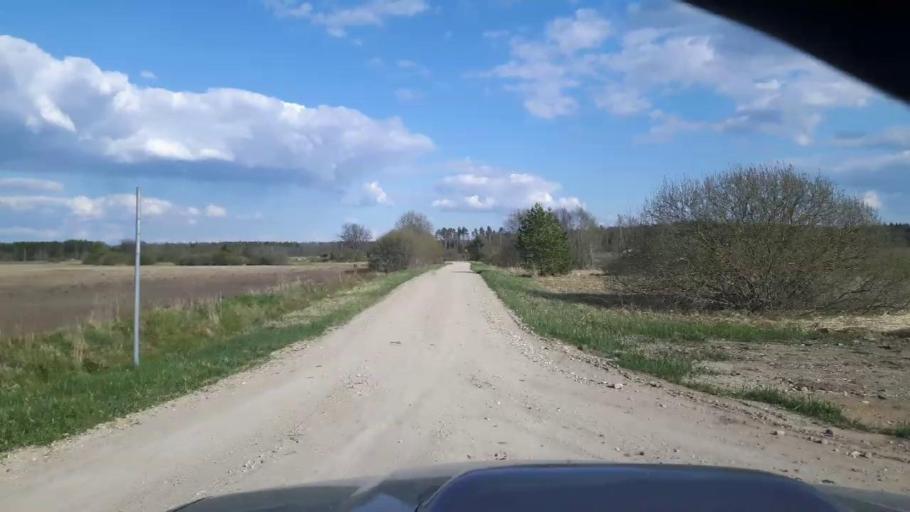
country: EE
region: Paernumaa
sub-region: Tootsi vald
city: Tootsi
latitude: 58.4139
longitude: 24.8395
